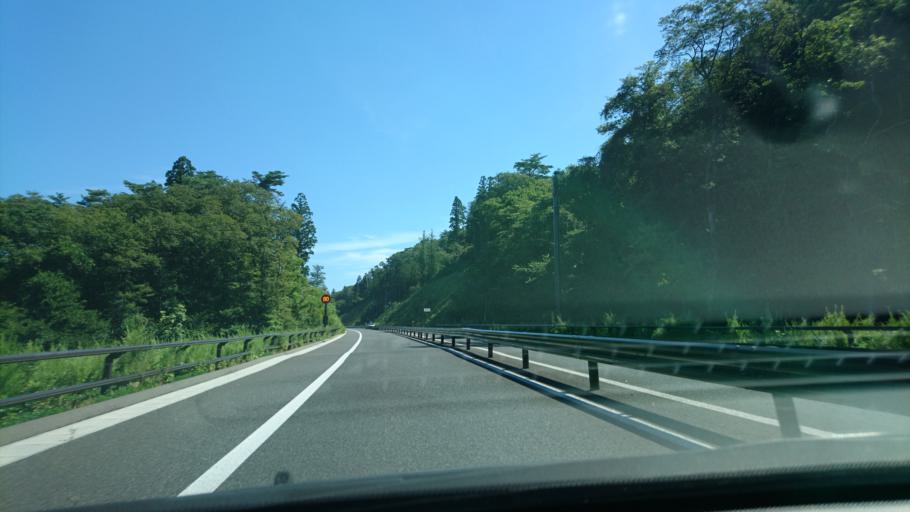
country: JP
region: Iwate
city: Tono
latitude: 39.3047
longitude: 141.4373
